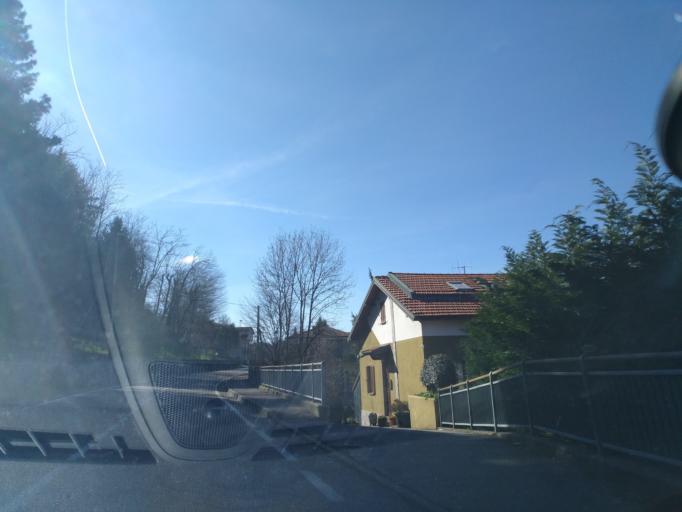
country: IT
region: Lombardy
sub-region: Provincia di Como
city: Lipomo
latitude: 45.7922
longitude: 9.1267
